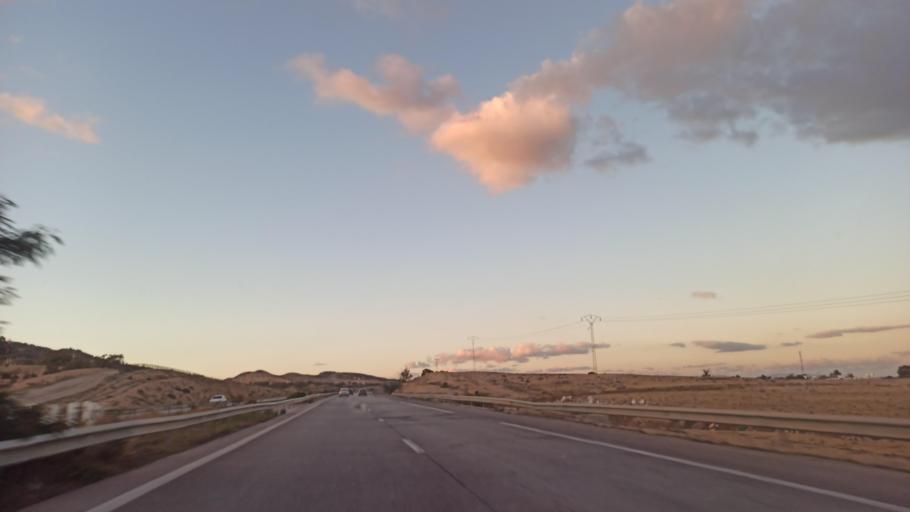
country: TN
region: Susah
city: Harqalah
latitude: 36.2260
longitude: 10.4150
